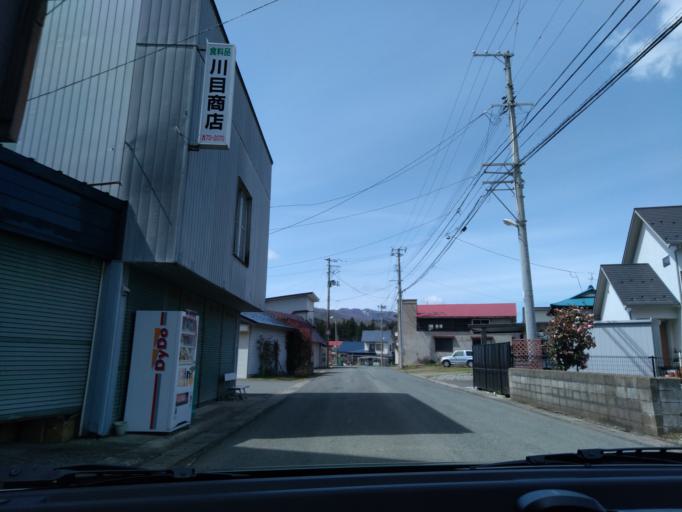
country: JP
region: Iwate
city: Kitakami
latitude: 39.3065
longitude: 140.9738
